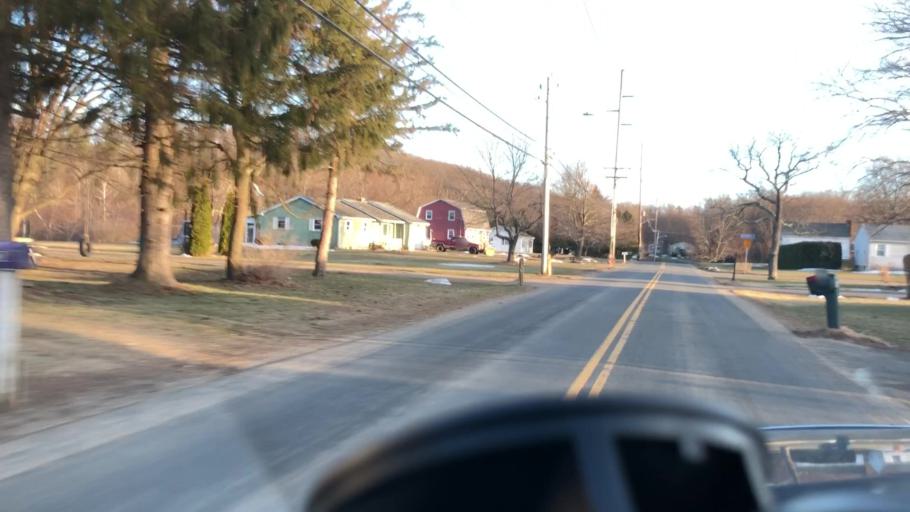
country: US
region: Massachusetts
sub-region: Hampshire County
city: Southampton
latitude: 42.2047
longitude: -72.6801
